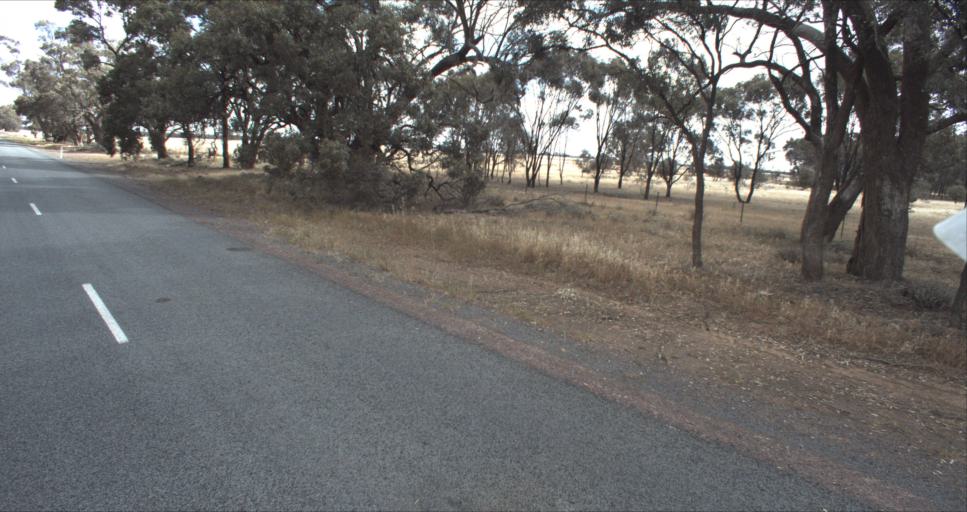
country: AU
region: New South Wales
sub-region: Leeton
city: Leeton
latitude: -34.6667
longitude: 146.3483
